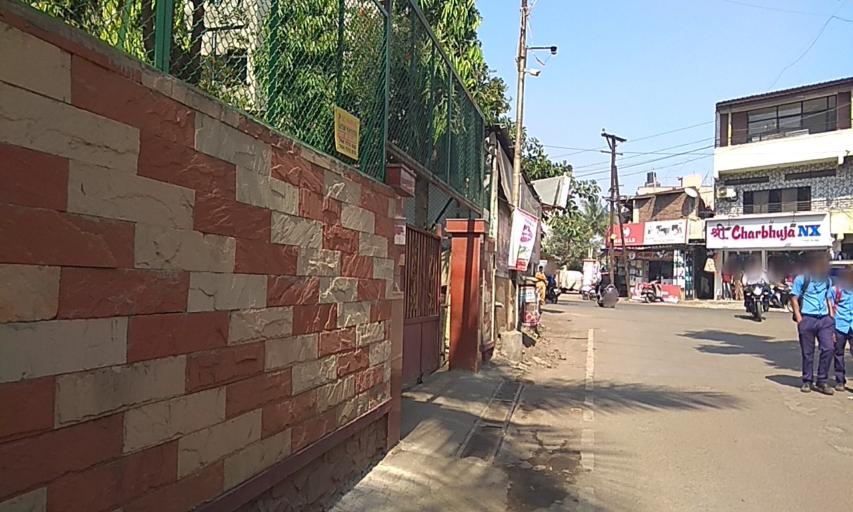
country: IN
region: Maharashtra
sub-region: Pune Division
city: Lohogaon
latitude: 18.5535
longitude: 73.9357
